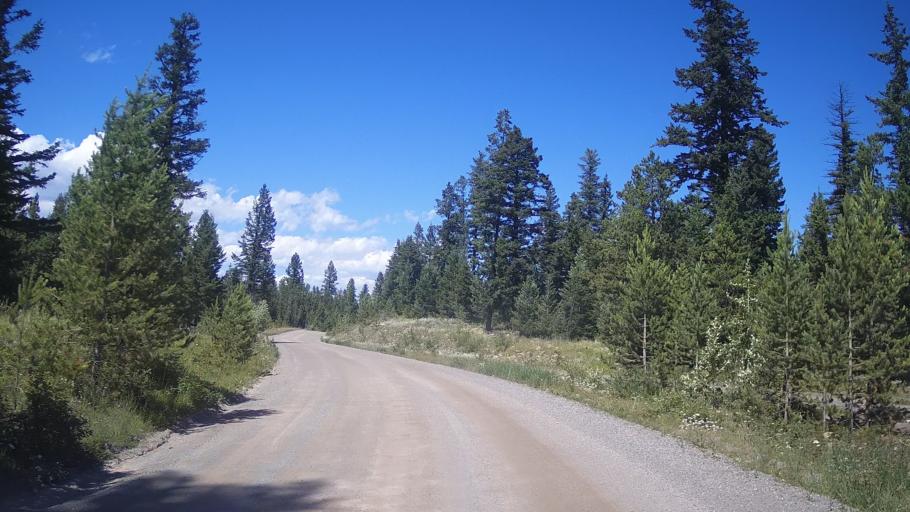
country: CA
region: British Columbia
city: Cache Creek
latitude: 51.1646
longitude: -121.5605
